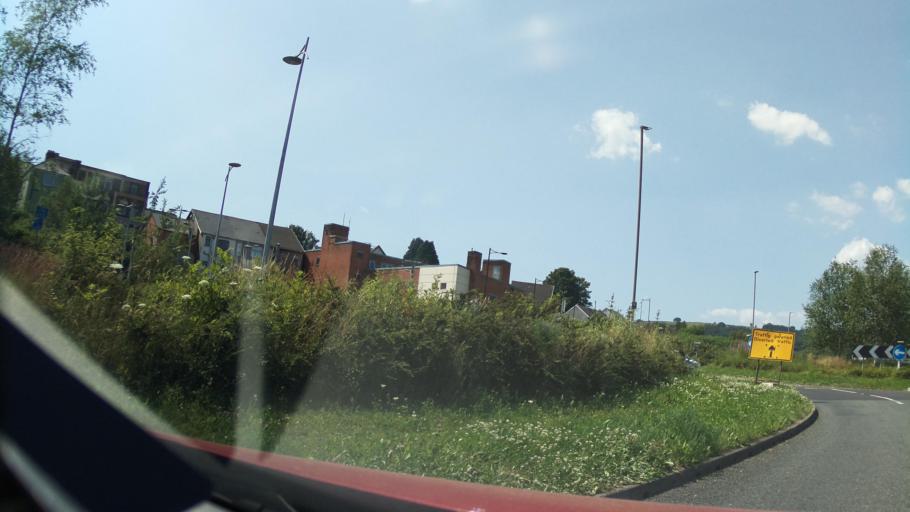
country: GB
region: Wales
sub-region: Caerphilly County Borough
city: Bargoed
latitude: 51.6916
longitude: -3.2282
